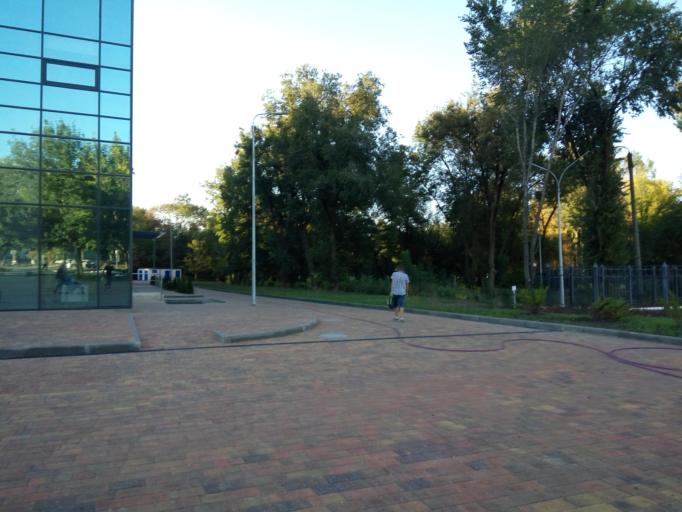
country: RU
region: Rostov
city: Rostov-na-Donu
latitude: 47.2421
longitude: 39.7588
